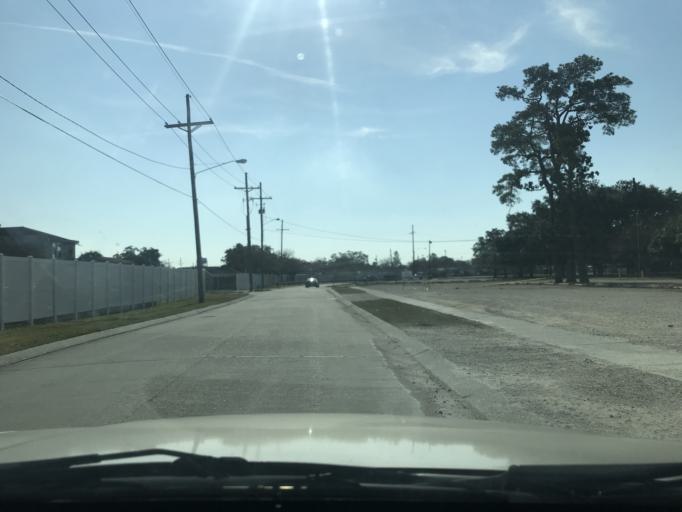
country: US
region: Louisiana
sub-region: Jefferson Parish
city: Marrero
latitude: 29.8910
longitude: -90.0930
